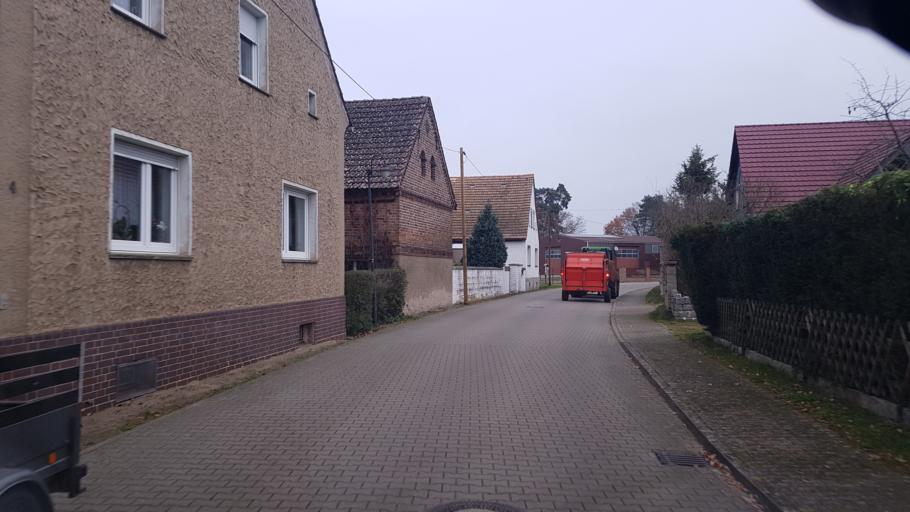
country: DE
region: Brandenburg
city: Schenkendobern
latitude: 51.9645
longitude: 14.6525
